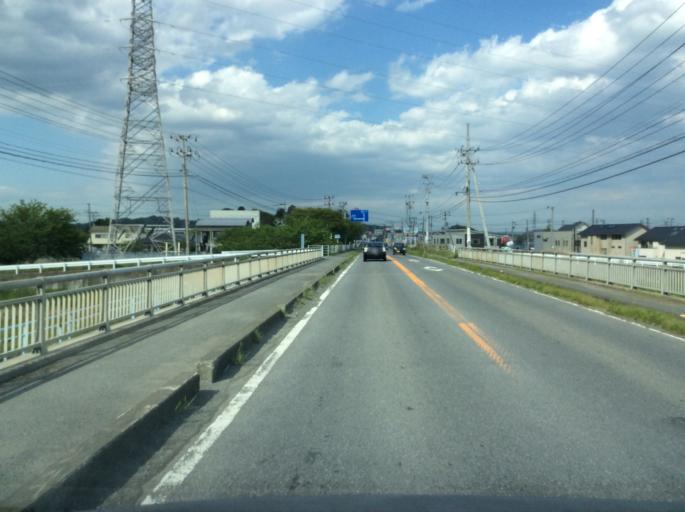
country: JP
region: Fukushima
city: Iwaki
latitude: 36.9441
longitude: 140.8555
